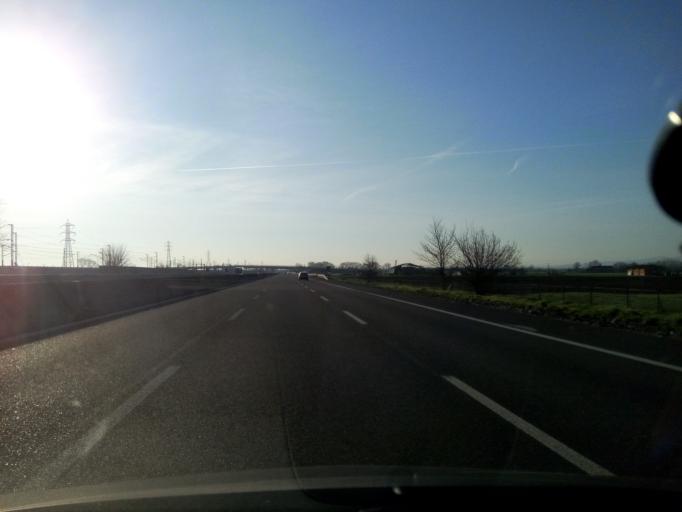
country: IT
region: Emilia-Romagna
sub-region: Provincia di Piacenza
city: Alseno
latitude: 44.9100
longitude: 10.0200
